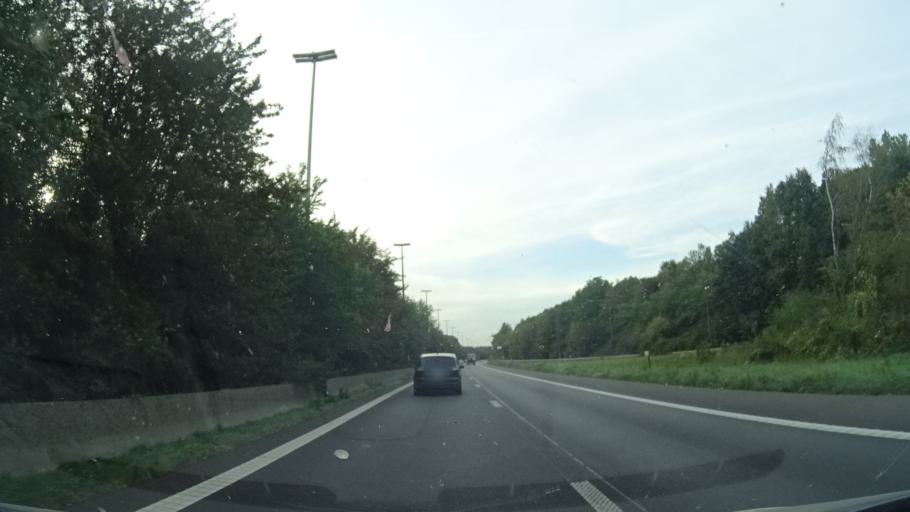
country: BE
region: Wallonia
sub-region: Province du Hainaut
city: Bernissart
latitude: 50.4881
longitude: 3.7009
